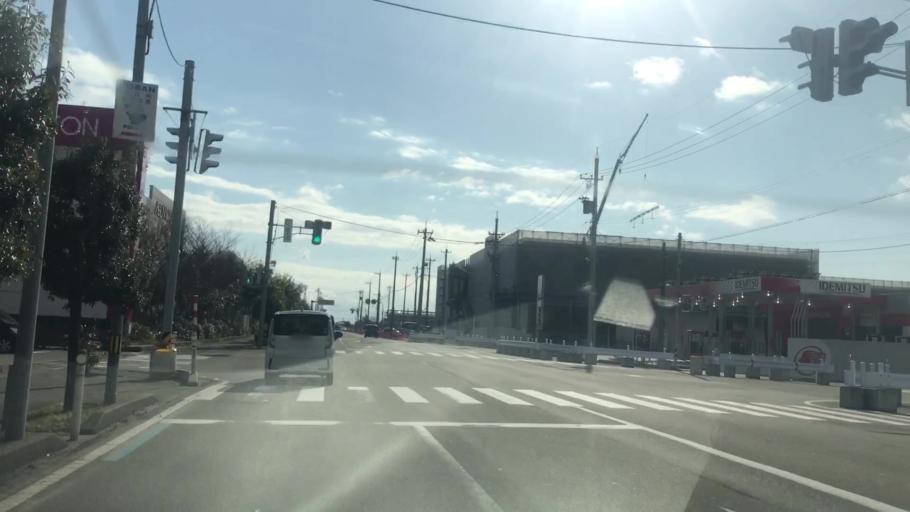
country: JP
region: Toyama
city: Takaoka
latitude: 36.7256
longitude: 137.0151
